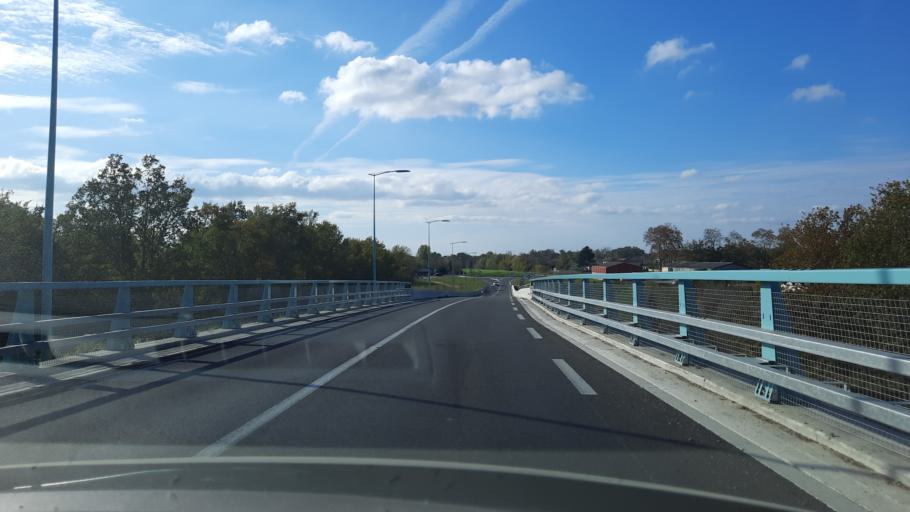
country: FR
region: Midi-Pyrenees
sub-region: Departement du Tarn-et-Garonne
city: Montauban
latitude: 44.0415
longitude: 1.3609
